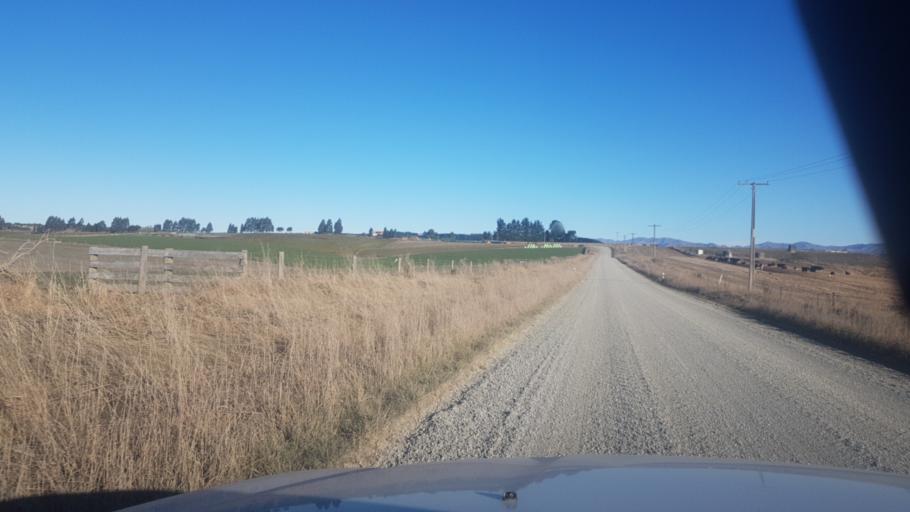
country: NZ
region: Canterbury
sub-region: Timaru District
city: Pleasant Point
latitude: -44.3528
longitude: 171.0711
